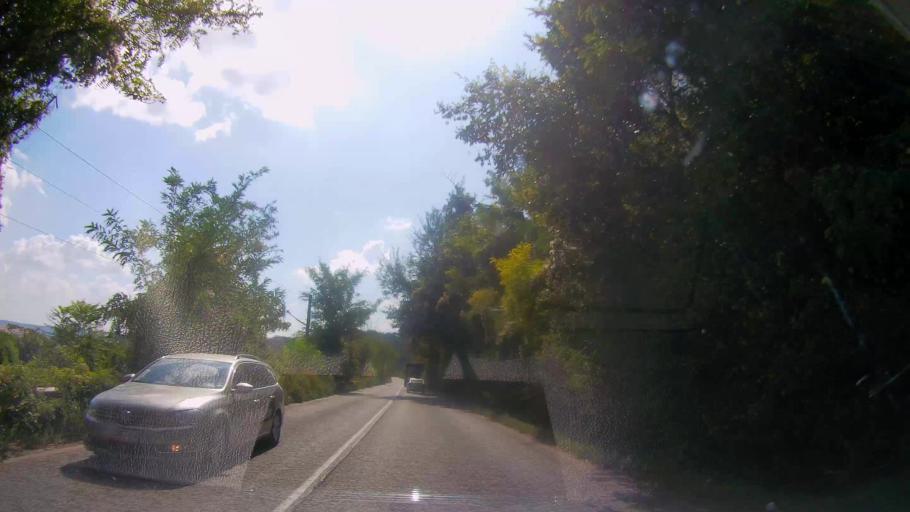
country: BG
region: Veliko Turnovo
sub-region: Obshtina Polski Trumbesh
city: Polski Trumbesh
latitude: 43.4362
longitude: 25.6547
